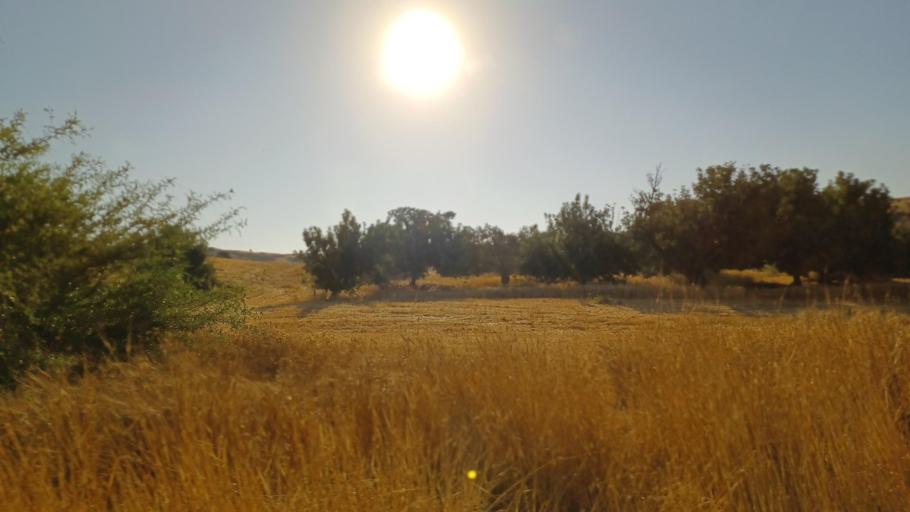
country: CY
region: Larnaka
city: Troulloi
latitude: 35.0301
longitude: 33.6271
